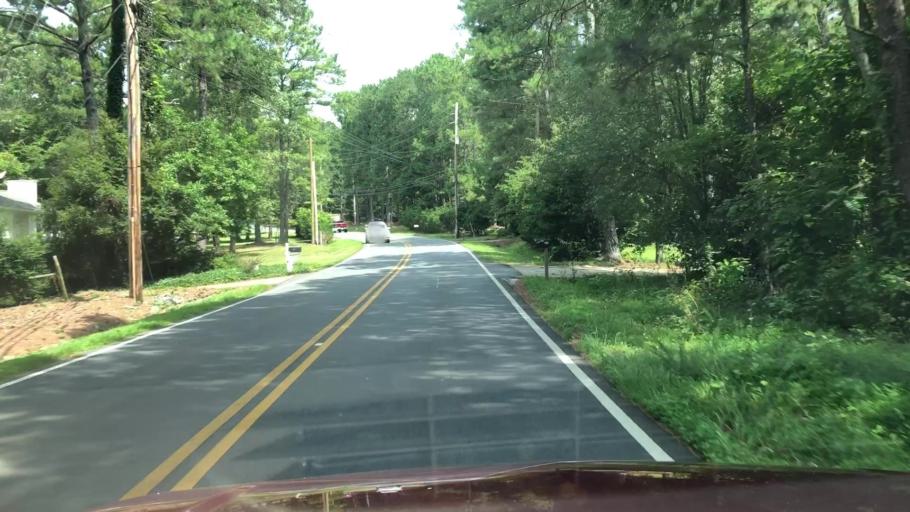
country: US
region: Georgia
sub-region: Cherokee County
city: Woodstock
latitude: 34.1496
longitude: -84.5936
